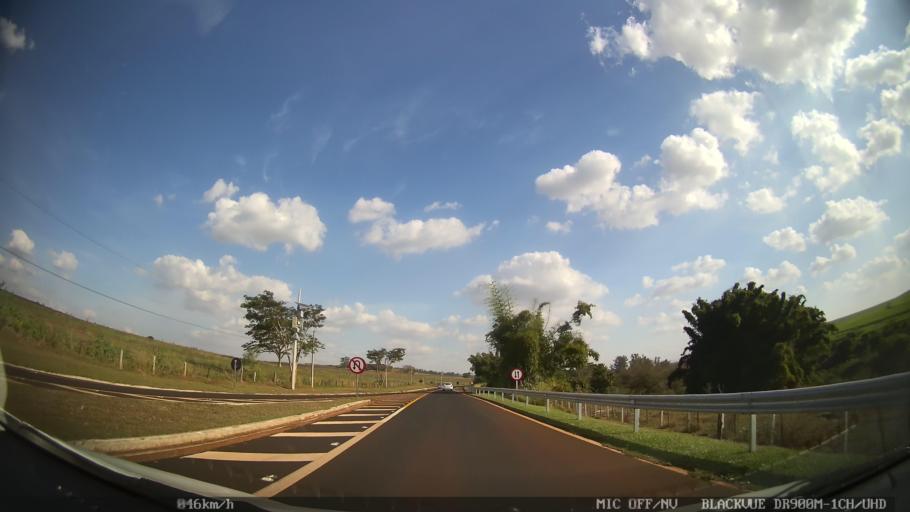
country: BR
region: Sao Paulo
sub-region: Ribeirao Preto
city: Ribeirao Preto
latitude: -21.1886
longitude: -47.8648
